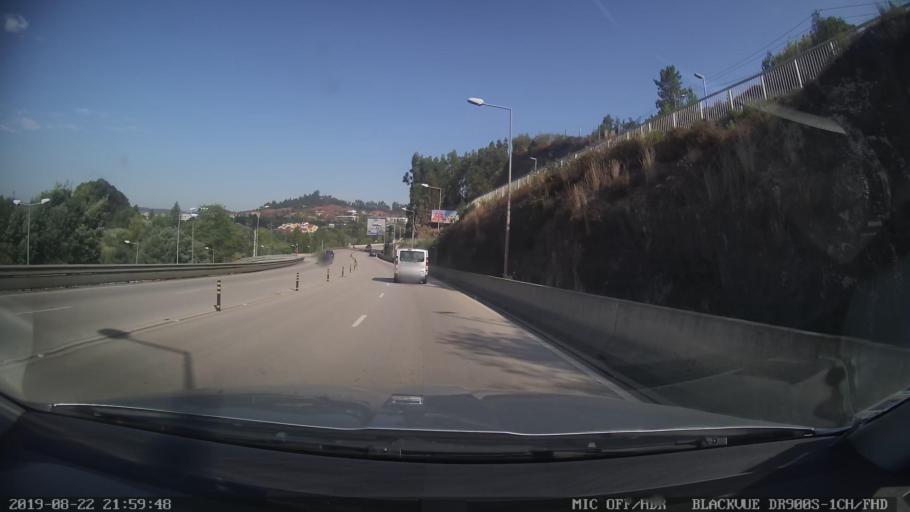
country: PT
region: Coimbra
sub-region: Coimbra
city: Coimbra
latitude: 40.1825
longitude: -8.3941
